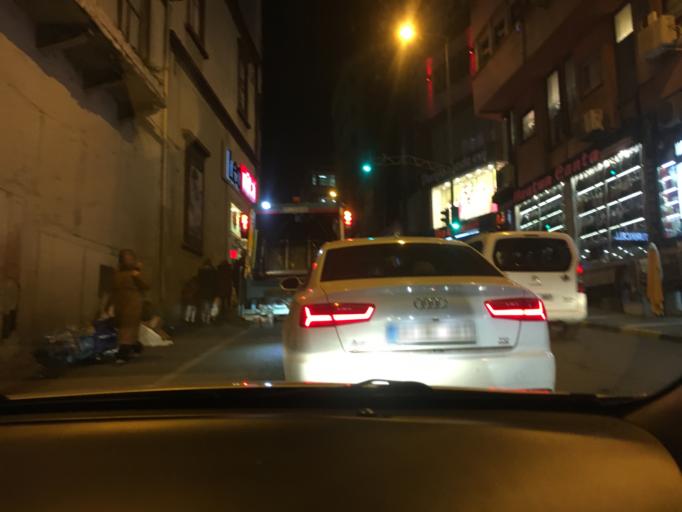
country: TR
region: Trabzon
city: Trabzon
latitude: 41.0068
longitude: 39.7257
